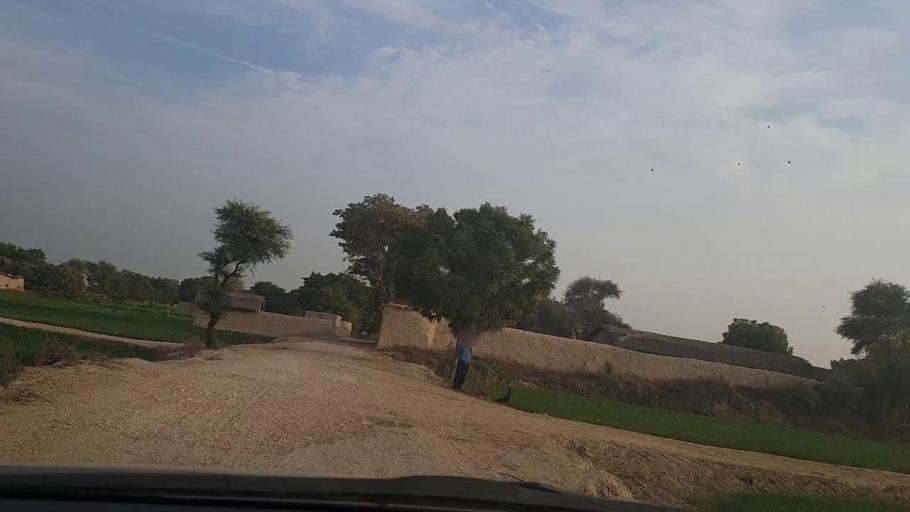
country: PK
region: Sindh
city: Daulatpur
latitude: 26.3318
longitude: 68.0235
